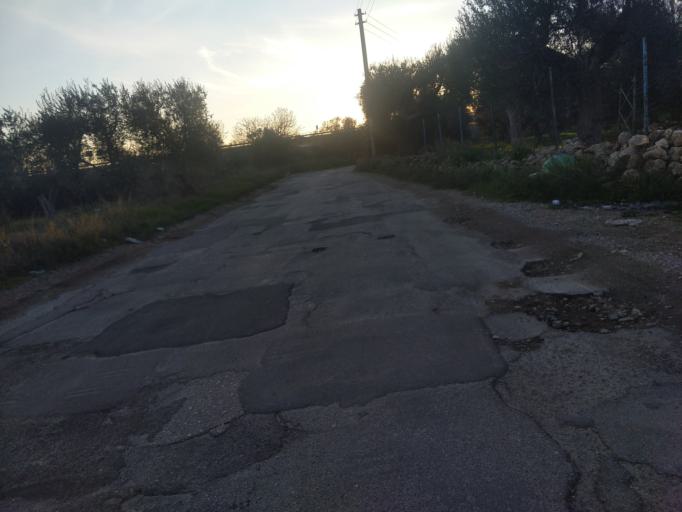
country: IT
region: Apulia
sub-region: Provincia di Bari
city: Modugno
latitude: 41.0877
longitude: 16.8055
